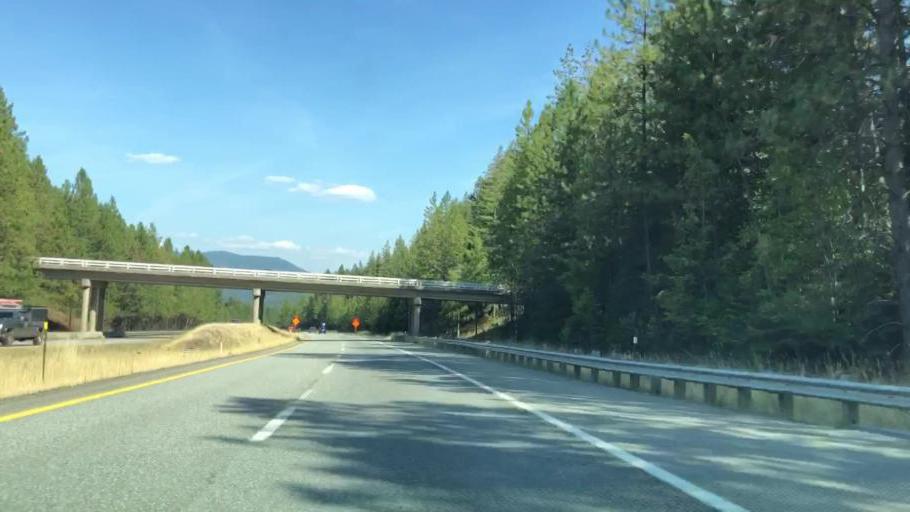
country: US
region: Idaho
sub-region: Shoshone County
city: Pinehurst
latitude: 47.5505
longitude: -116.2961
